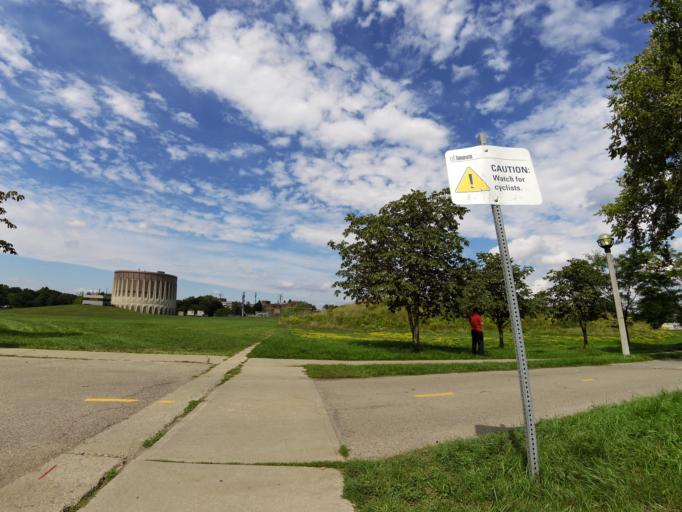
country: CA
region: Ontario
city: Toronto
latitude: 43.6619
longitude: -79.3173
